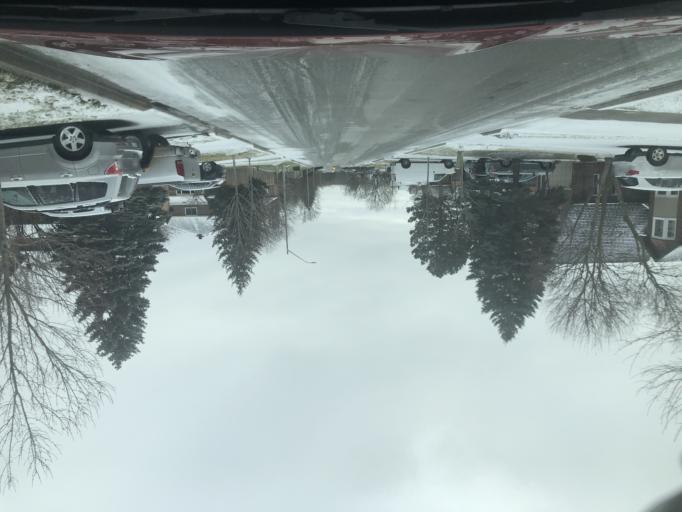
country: CA
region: Ontario
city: Markham
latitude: 43.8715
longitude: -79.2373
